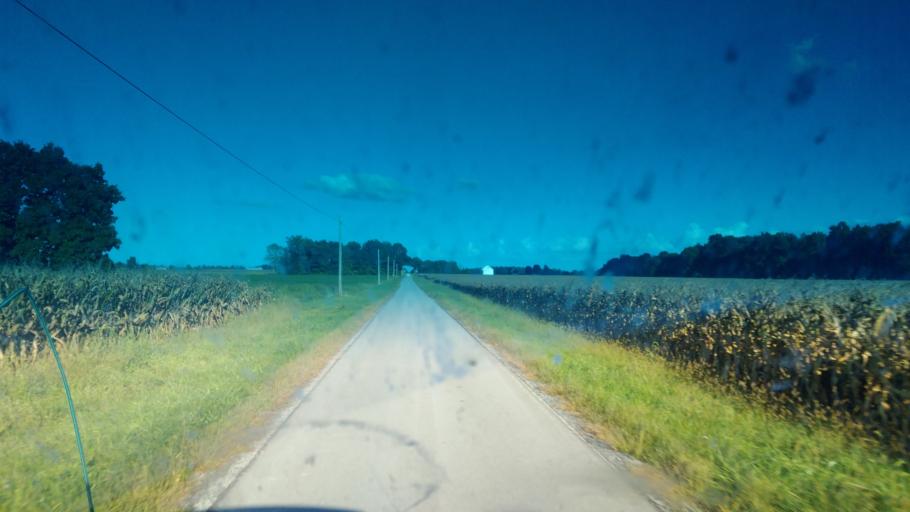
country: US
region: Ohio
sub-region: Wyandot County
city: Carey
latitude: 40.9411
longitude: -83.4820
